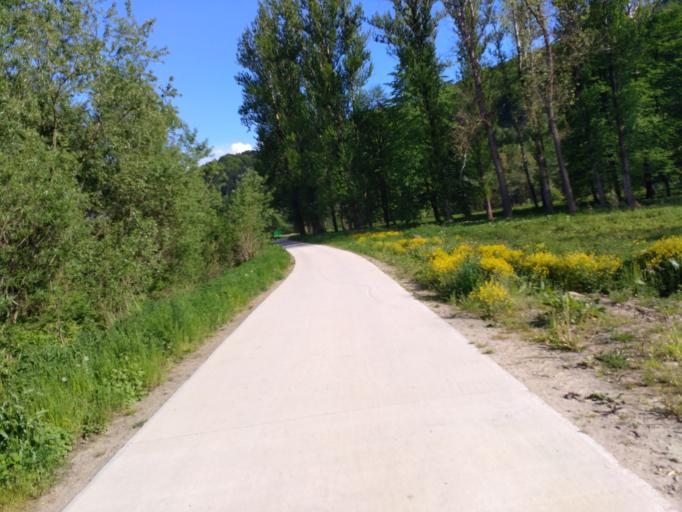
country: PL
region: Lesser Poland Voivodeship
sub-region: Powiat nowosadecki
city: Lacko
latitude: 49.5504
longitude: 20.4432
